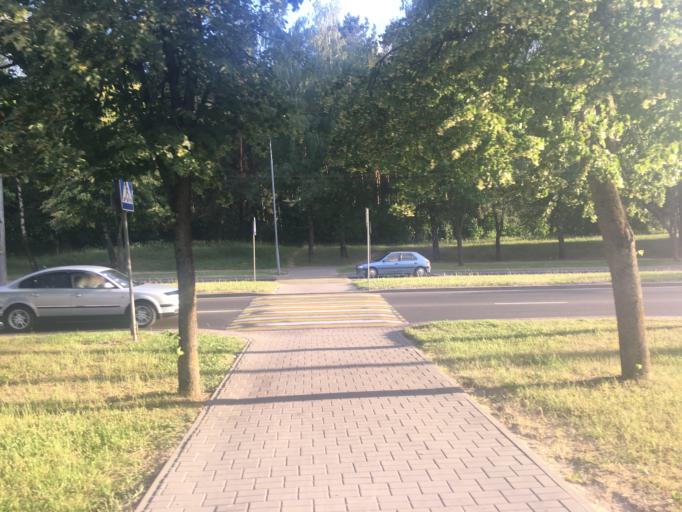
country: BY
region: Grodnenskaya
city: Hrodna
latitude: 53.6837
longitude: 23.8062
